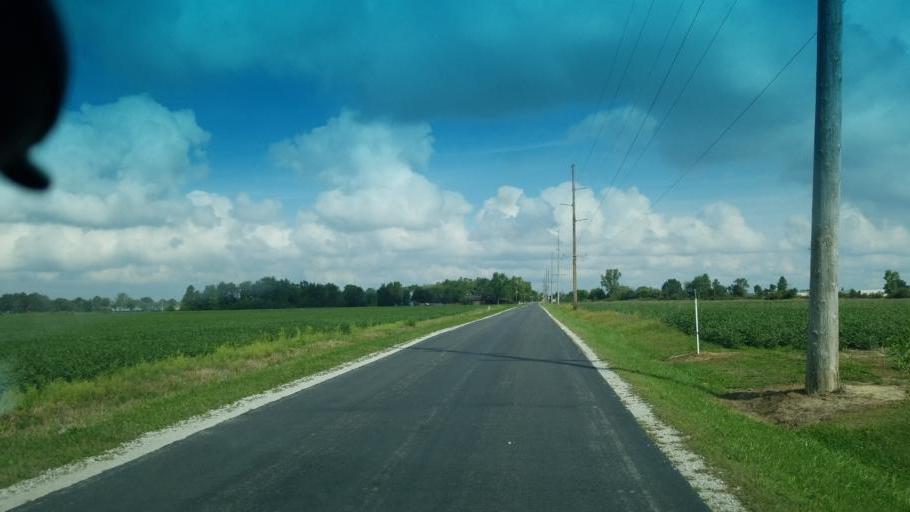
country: US
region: Ohio
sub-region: Wyandot County
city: Carey
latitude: 40.9365
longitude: -83.3674
